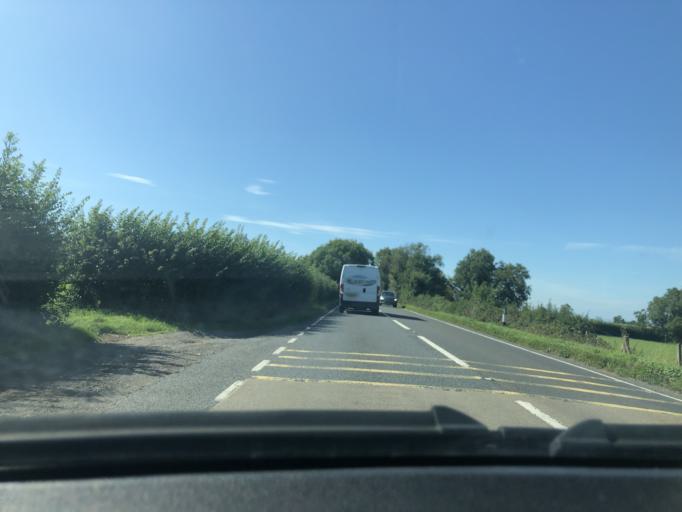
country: GB
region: England
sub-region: Somerset
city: Westonzoyland
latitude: 51.1390
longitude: -2.8690
